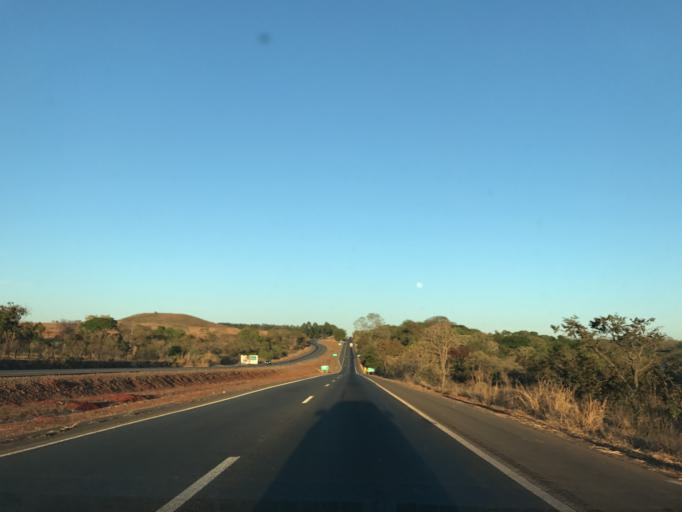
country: BR
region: Goias
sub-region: Anapolis
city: Anapolis
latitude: -16.3133
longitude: -48.8359
